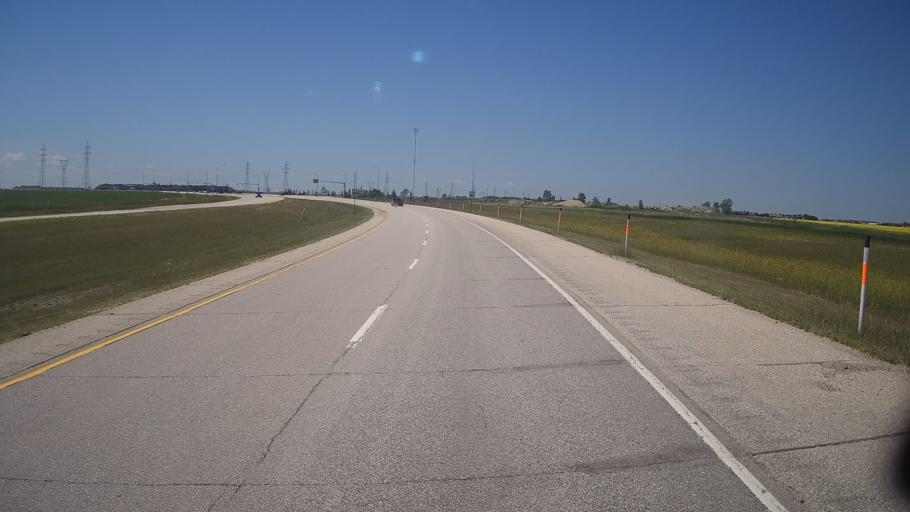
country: CA
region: Manitoba
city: Stonewall
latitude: 49.9898
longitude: -97.3032
